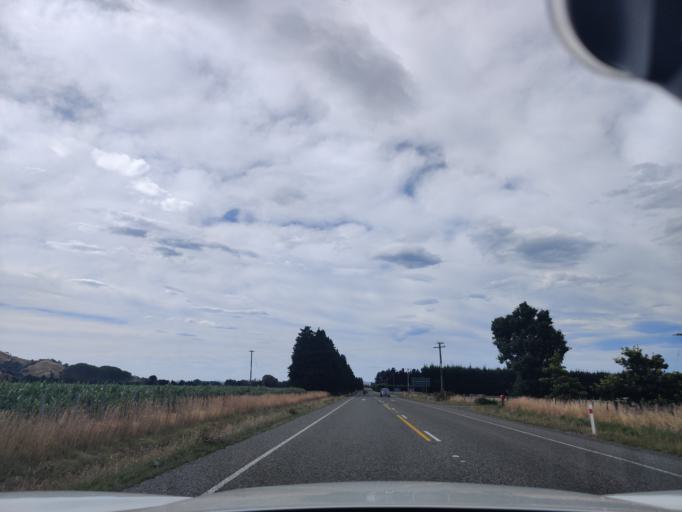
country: NZ
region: Wellington
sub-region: Masterton District
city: Masterton
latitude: -40.8571
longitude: 175.6398
